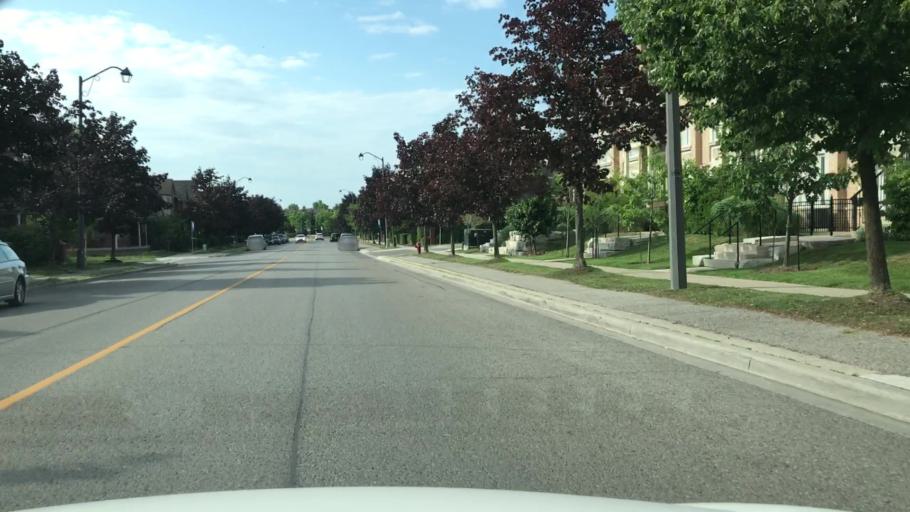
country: CA
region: Ontario
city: Newmarket
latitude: 44.0094
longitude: -79.4503
